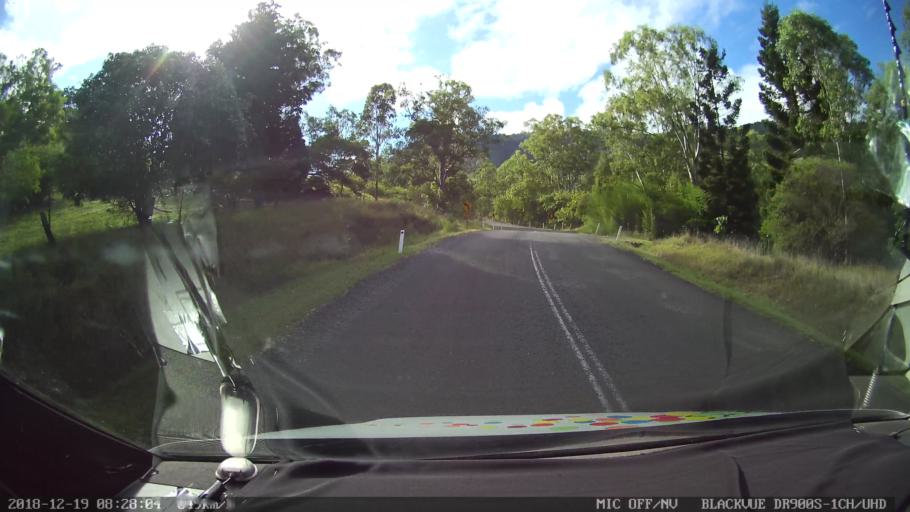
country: AU
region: New South Wales
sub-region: Kyogle
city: Kyogle
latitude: -28.3209
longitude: 152.9297
